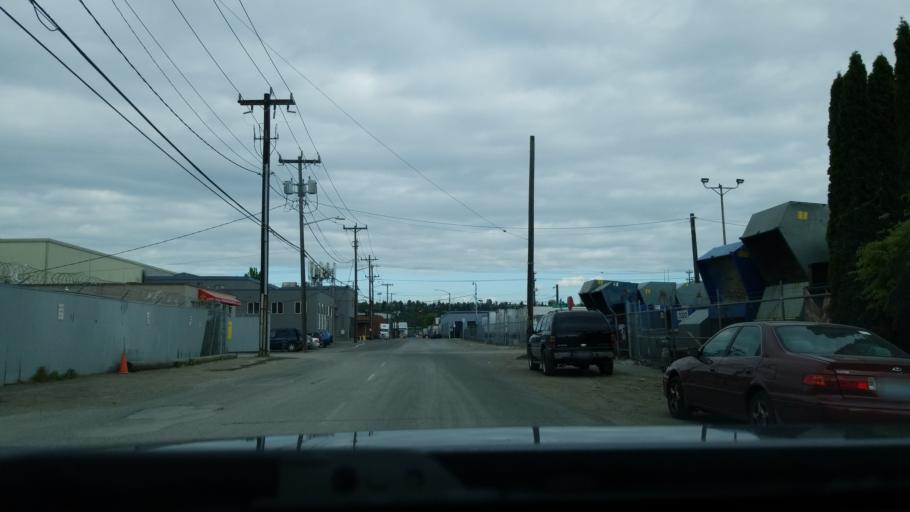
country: US
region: Washington
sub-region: King County
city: White Center
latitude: 47.5574
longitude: -122.3361
